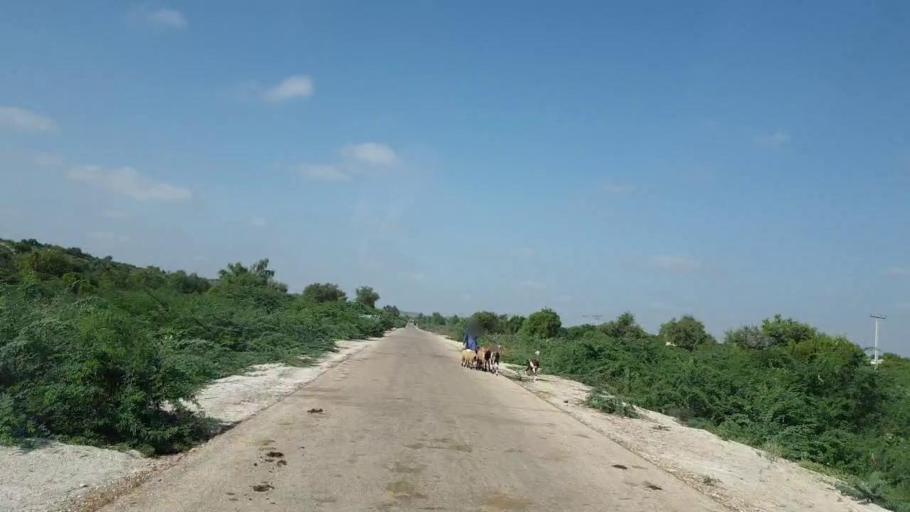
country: PK
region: Sindh
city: Mithi
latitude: 24.5323
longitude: 69.8438
